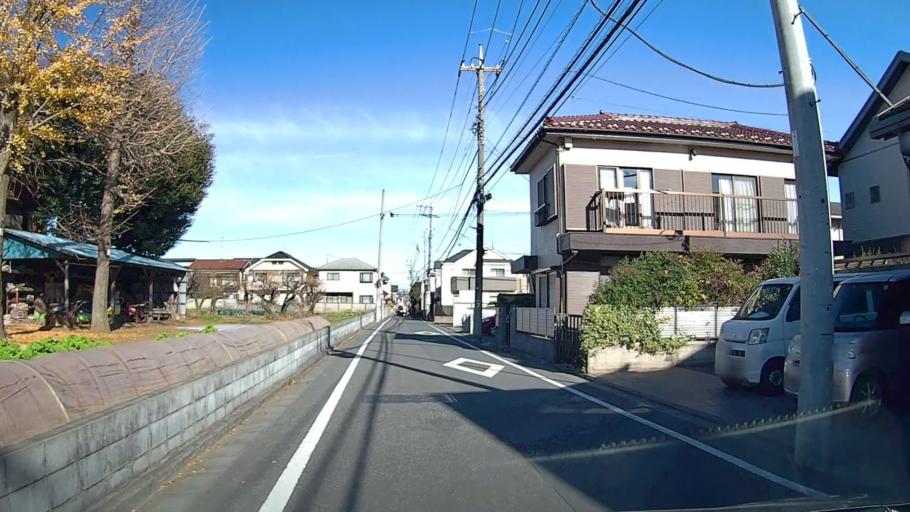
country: JP
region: Saitama
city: Wako
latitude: 35.7553
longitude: 139.6123
